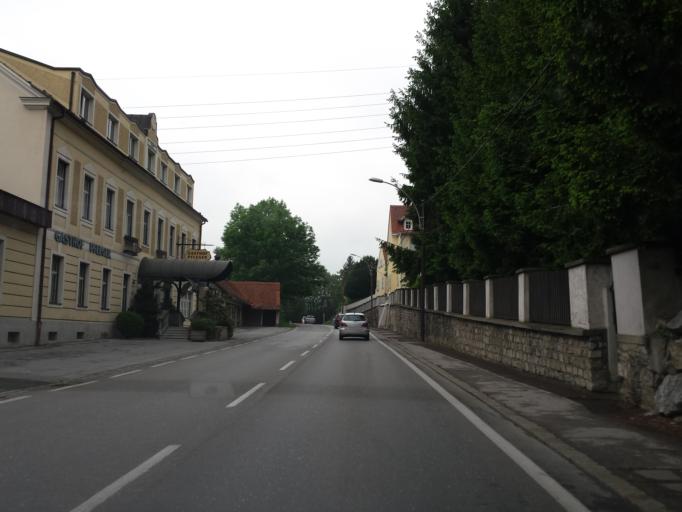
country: AT
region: Styria
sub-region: Graz Stadt
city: Goesting
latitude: 47.0969
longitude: 15.4236
